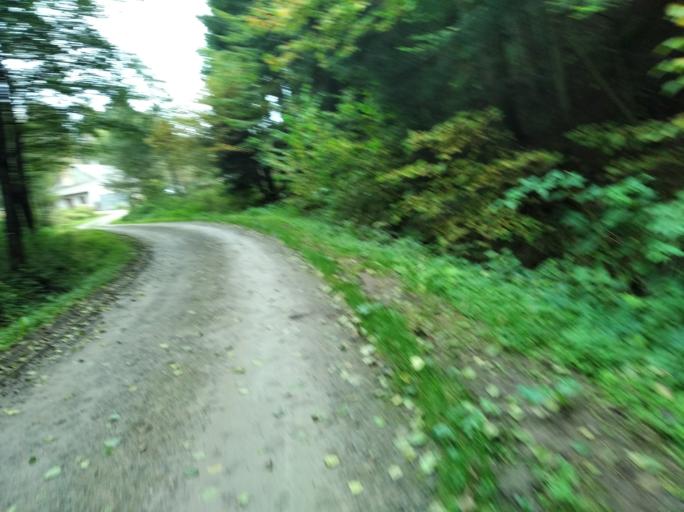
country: PL
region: Subcarpathian Voivodeship
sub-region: Powiat strzyzowski
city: Jawornik
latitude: 49.8323
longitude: 21.8953
